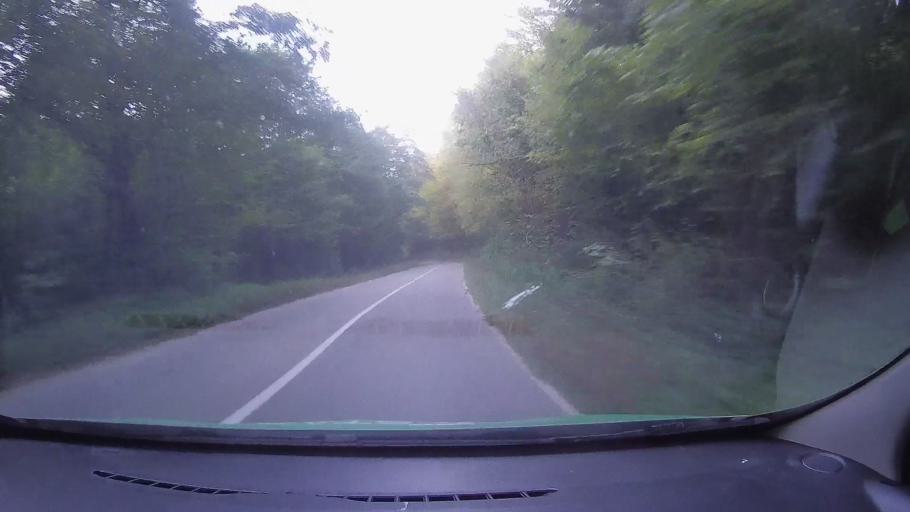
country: RO
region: Timis
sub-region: Comuna Fardea
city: Fardea
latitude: 45.6887
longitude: 22.1571
